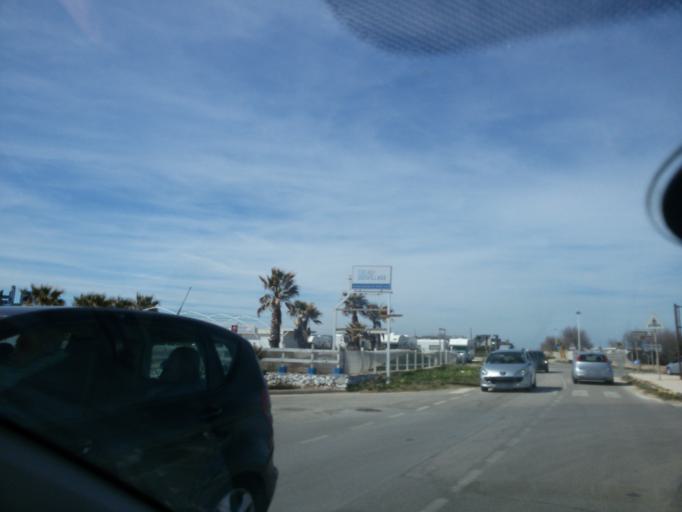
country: IT
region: Apulia
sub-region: Provincia di Brindisi
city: Pezze di Greco
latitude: 40.8437
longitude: 17.4638
